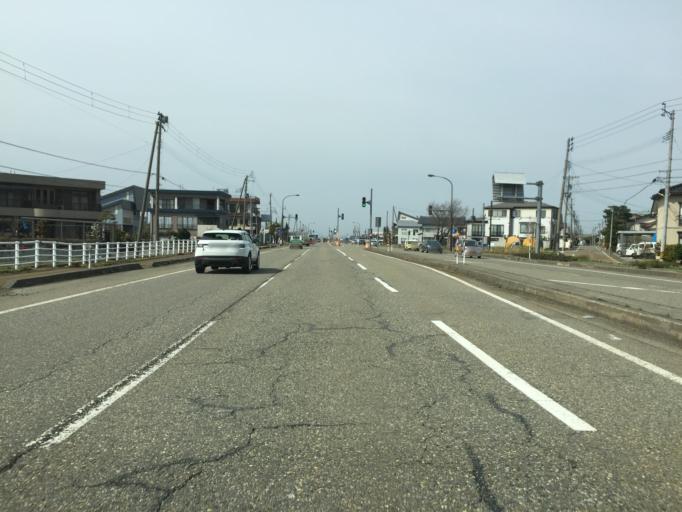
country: JP
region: Niigata
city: Ojiya
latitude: 37.3480
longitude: 138.8292
